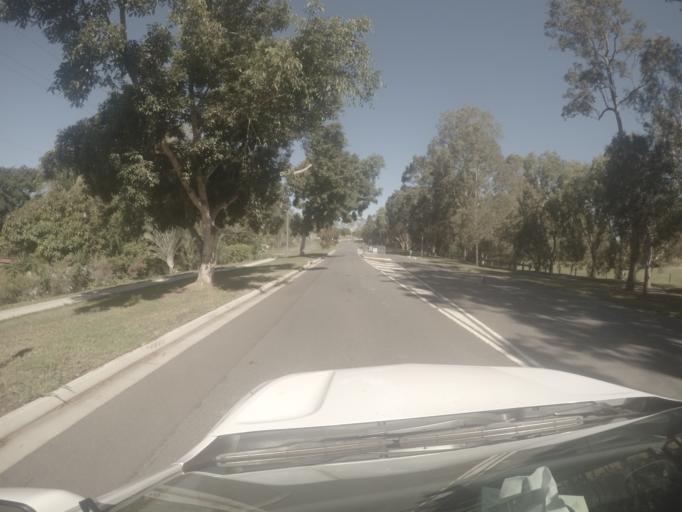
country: AU
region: Queensland
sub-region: Ipswich
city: Springfield
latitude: -27.6489
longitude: 152.9201
